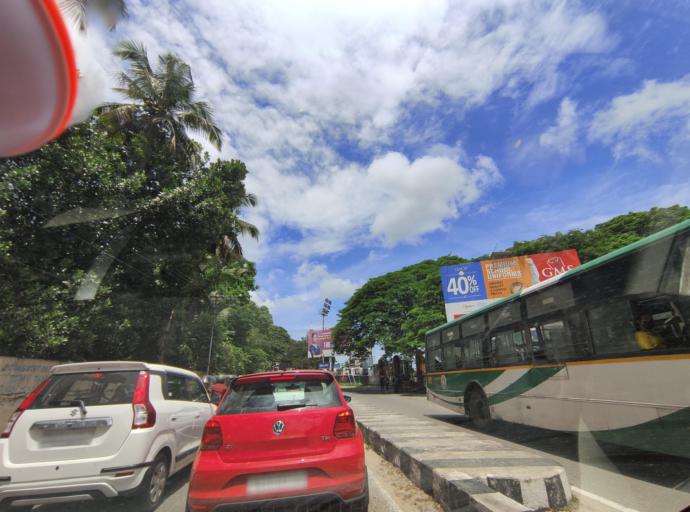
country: IN
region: Kerala
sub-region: Thiruvananthapuram
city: Thiruvananthapuram
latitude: 8.5061
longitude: 76.9509
